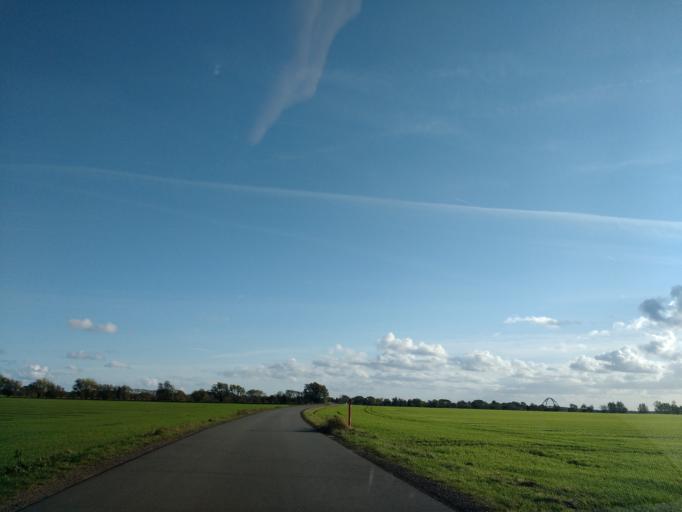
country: DE
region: Schleswig-Holstein
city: Grossenbrode
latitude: 54.4295
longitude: 11.1174
